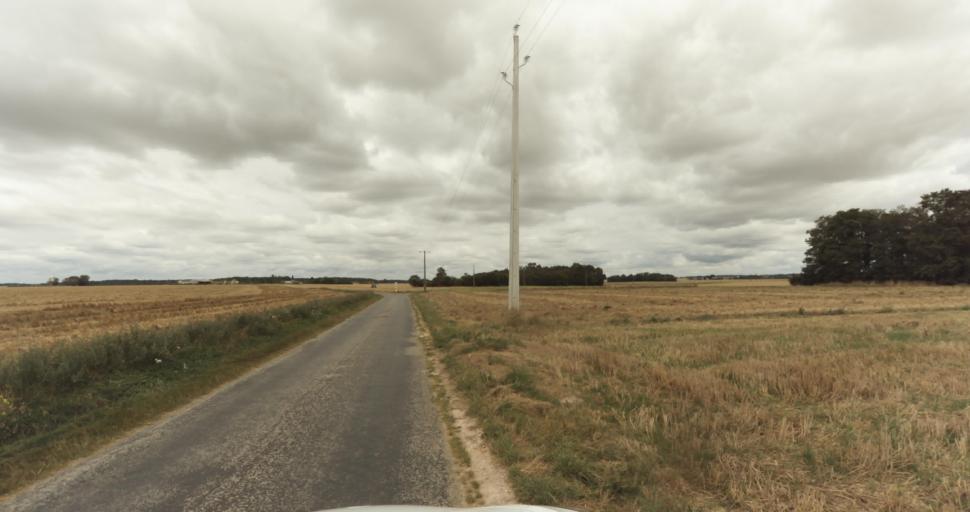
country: FR
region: Haute-Normandie
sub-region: Departement de l'Eure
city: Nonancourt
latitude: 48.7925
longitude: 1.1422
